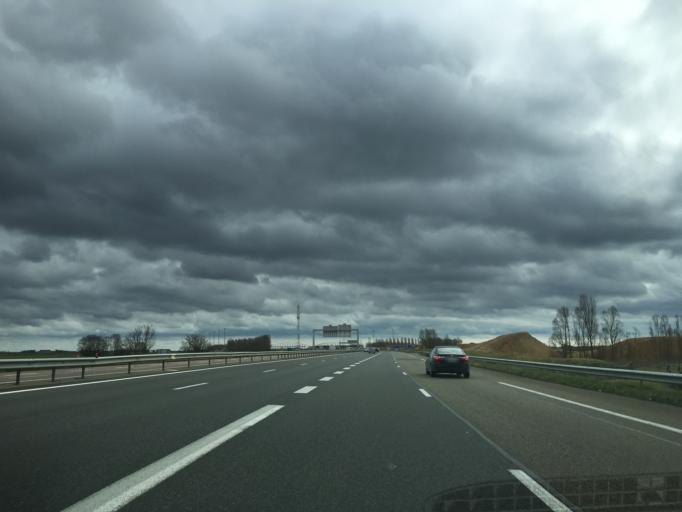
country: FR
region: Ile-de-France
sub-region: Departement de Seine-et-Marne
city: Voisenon
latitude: 48.5929
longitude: 2.6421
